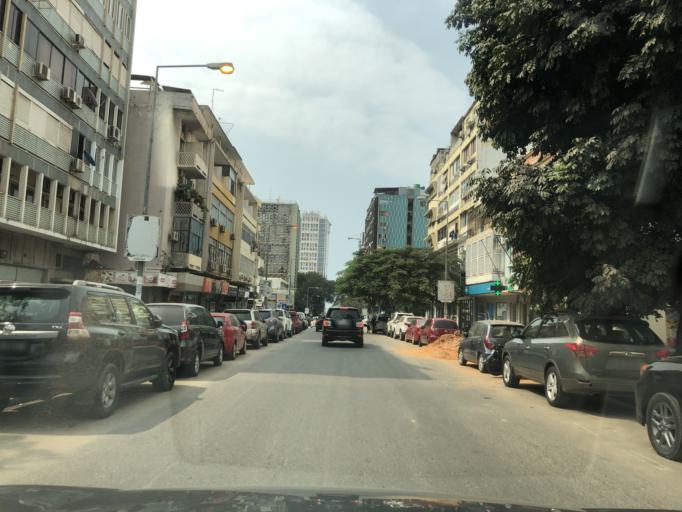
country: AO
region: Luanda
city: Luanda
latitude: -8.8172
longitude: 13.2319
